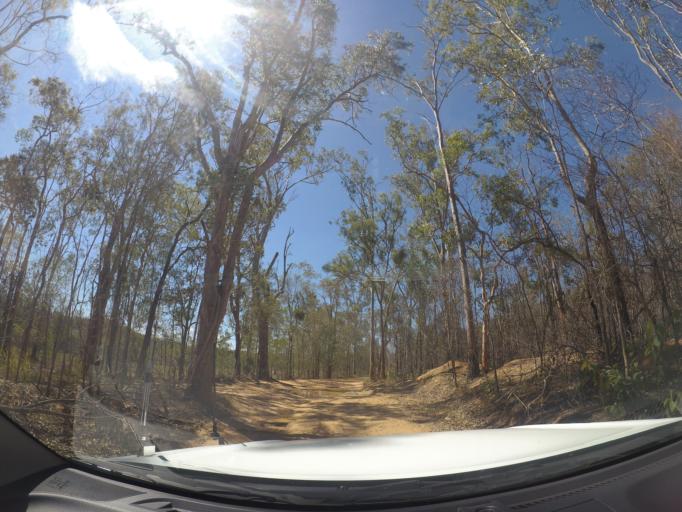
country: AU
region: Queensland
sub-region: Logan
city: North Maclean
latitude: -27.7774
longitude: 152.9367
